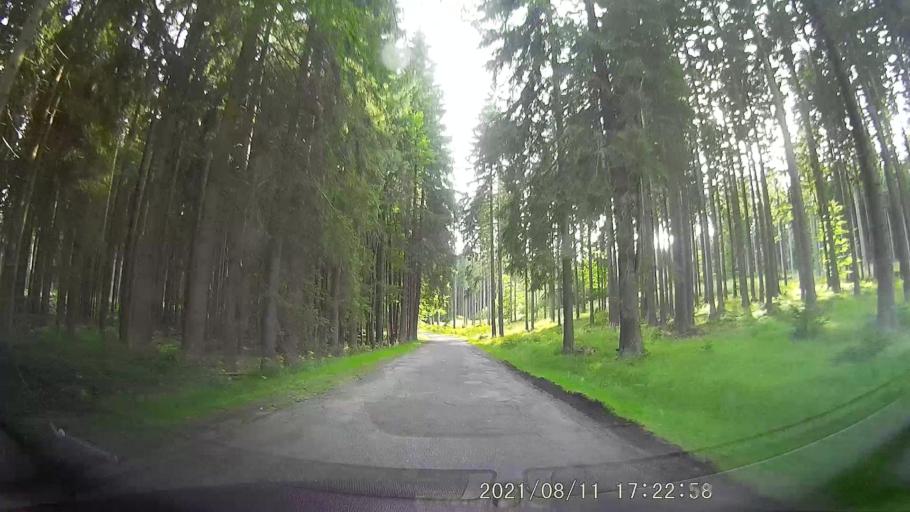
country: PL
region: Lower Silesian Voivodeship
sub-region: Powiat klodzki
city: Polanica-Zdroj
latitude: 50.3054
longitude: 16.5042
